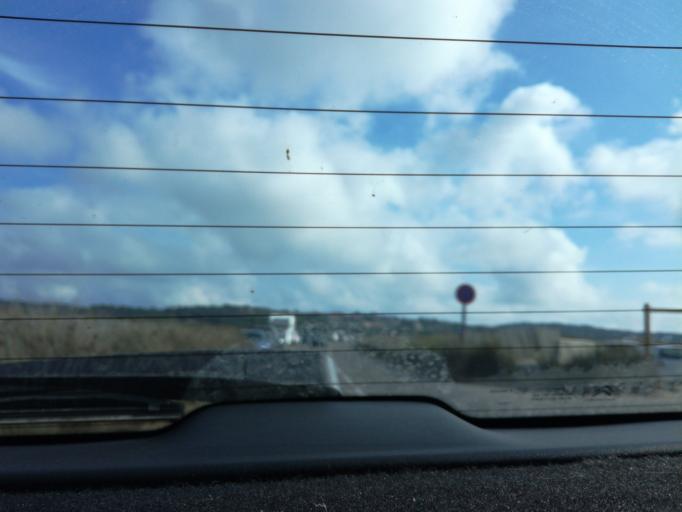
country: FR
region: Provence-Alpes-Cote d'Azur
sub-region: Departement du Var
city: Hyeres
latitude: 43.0519
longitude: 6.1333
